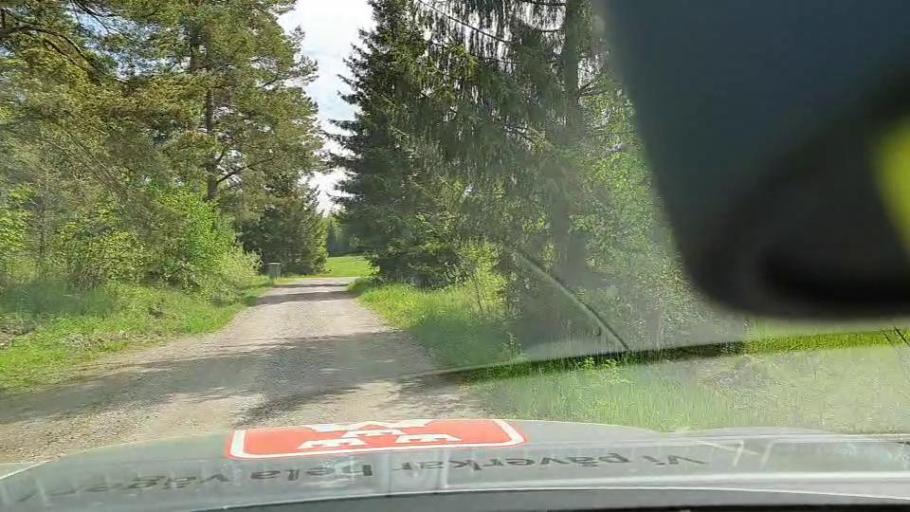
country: SE
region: Soedermanland
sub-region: Eskilstuna Kommun
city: Skogstorp
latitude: 59.2503
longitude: 16.5005
